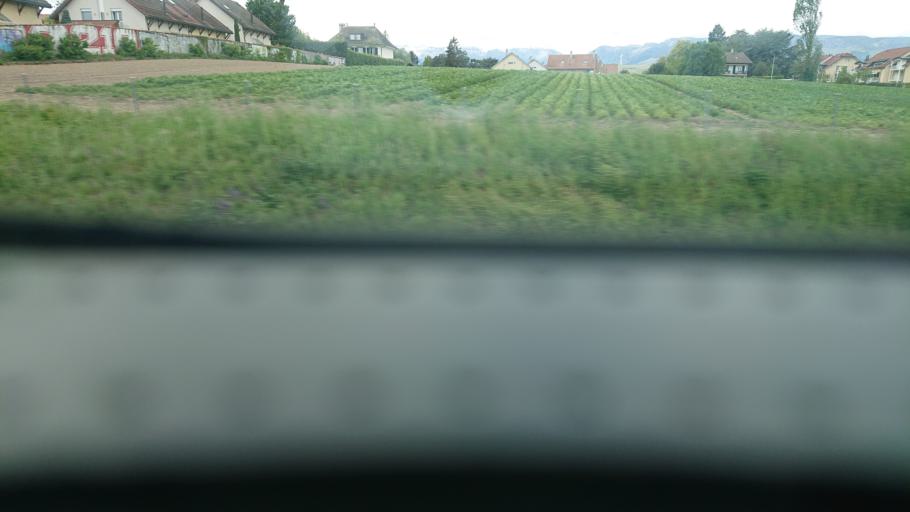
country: CH
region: Vaud
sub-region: Nyon District
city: Coppet
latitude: 46.3142
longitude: 6.1868
